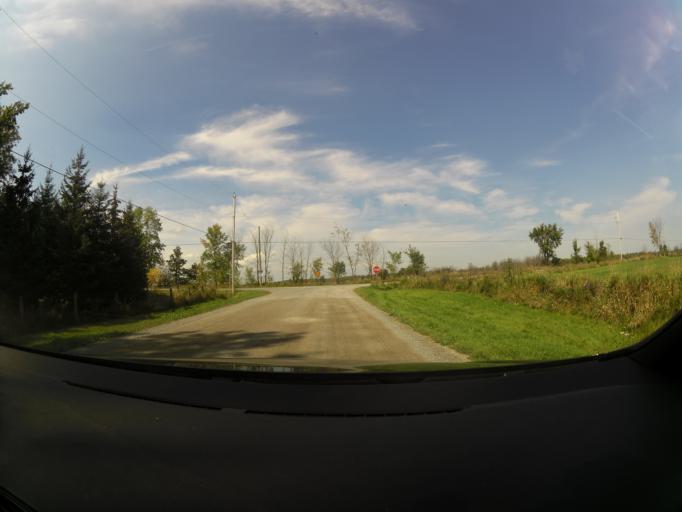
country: CA
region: Ontario
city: Carleton Place
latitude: 45.2868
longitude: -76.2362
